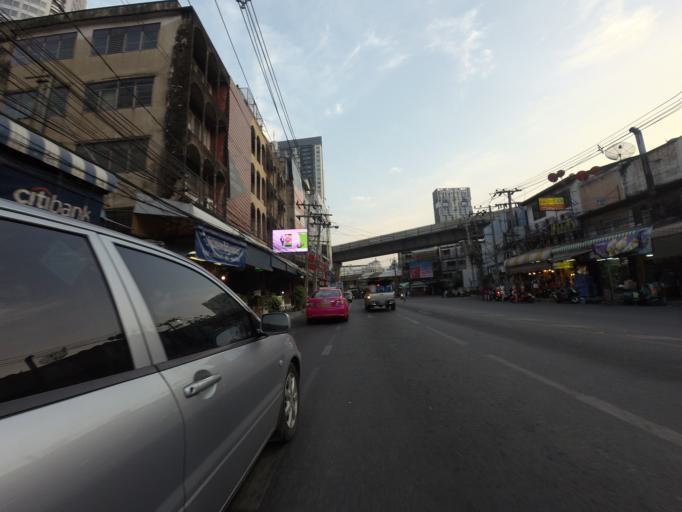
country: TH
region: Bangkok
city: Watthana
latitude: 13.7243
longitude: 100.5795
